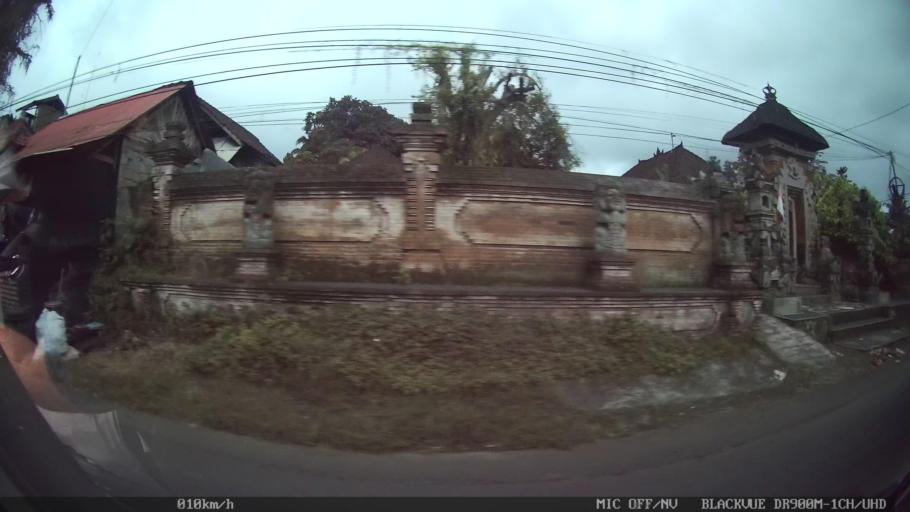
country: ID
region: Bali
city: Banjar Triwangsakeliki
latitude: -8.4500
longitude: 115.2622
